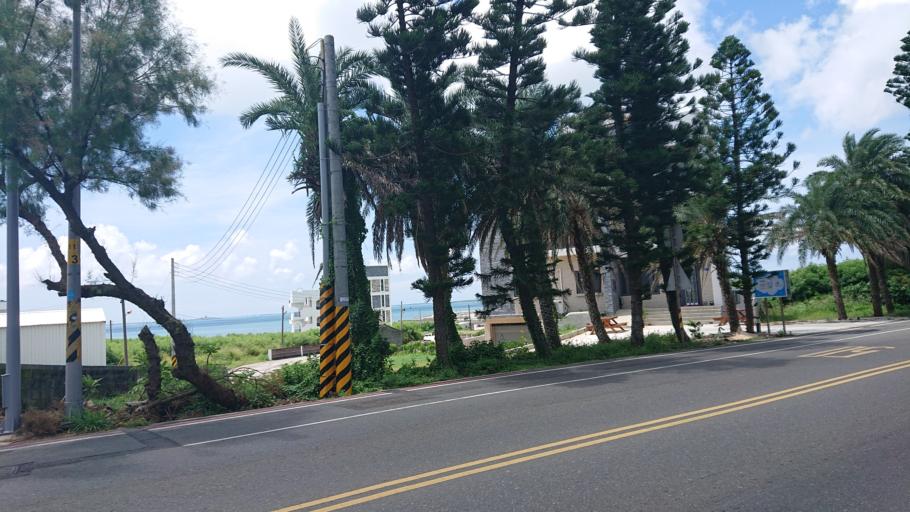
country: TW
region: Taiwan
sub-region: Penghu
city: Ma-kung
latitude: 23.5838
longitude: 119.6076
